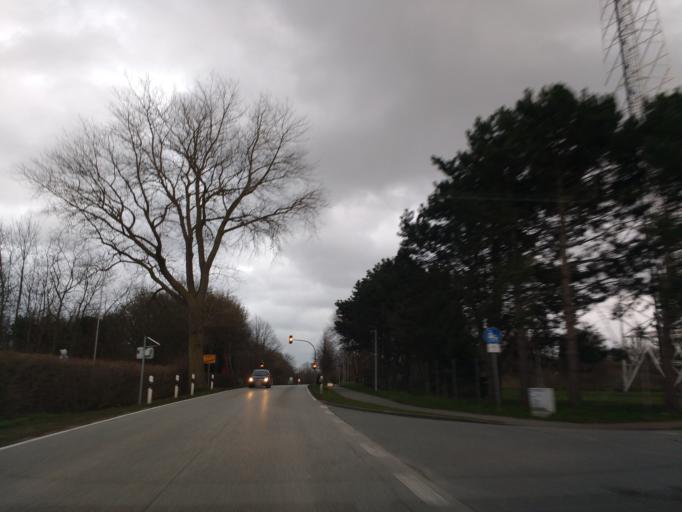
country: DE
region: Schleswig-Holstein
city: Heiligenhafen
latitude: 54.3666
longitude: 10.9974
